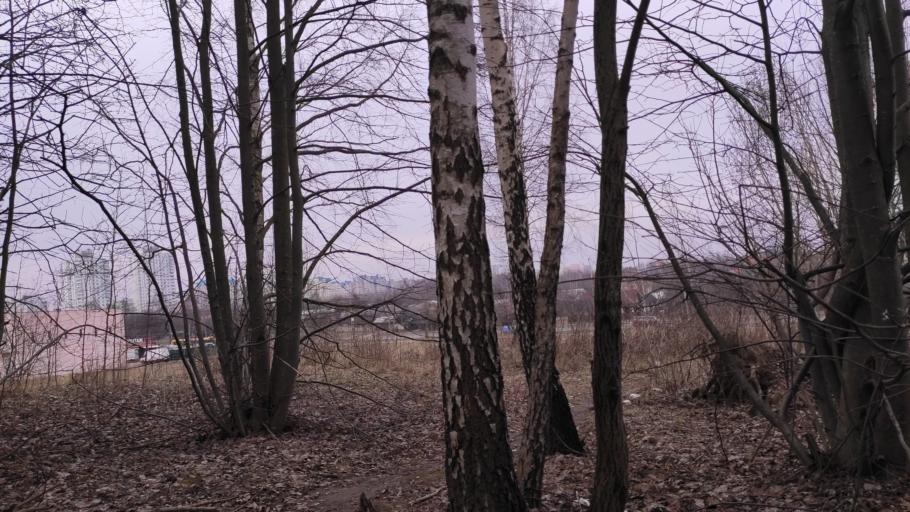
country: BY
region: Minsk
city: Novoye Medvezhino
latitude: 53.8926
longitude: 27.4706
